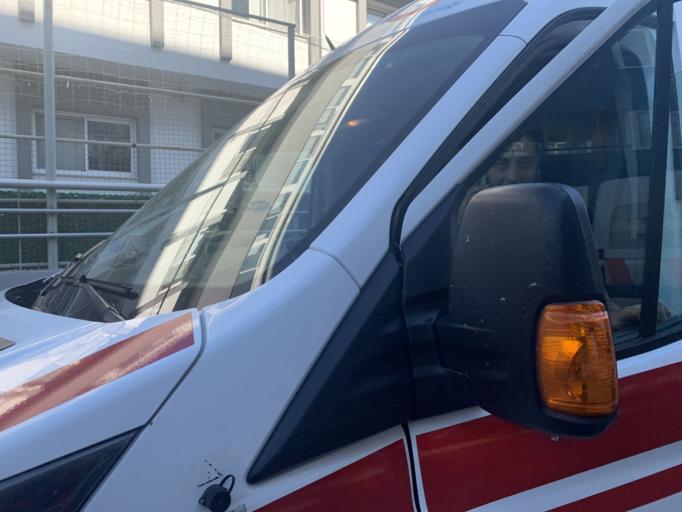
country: TR
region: Izmir
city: Bornova
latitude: 38.4589
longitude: 27.1944
